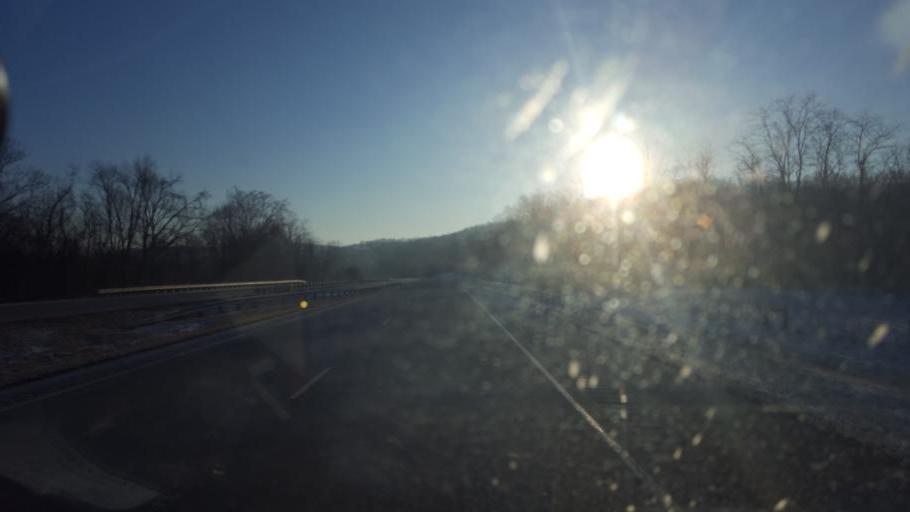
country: US
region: Ohio
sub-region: Pike County
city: Piketon
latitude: 39.0438
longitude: -83.1702
